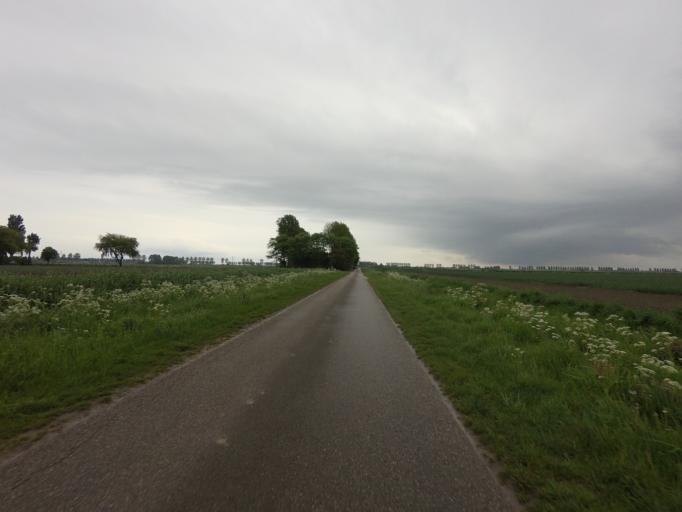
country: NL
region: South Holland
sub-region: Gemeente Goeree-Overflakkee
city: Middelharnis
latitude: 51.7236
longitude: 4.2152
